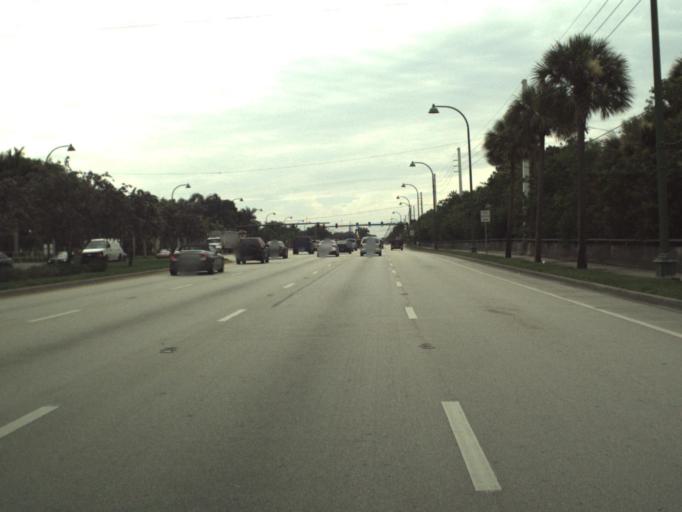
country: US
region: Florida
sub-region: Palm Beach County
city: Wellington
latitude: 26.6812
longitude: -80.2328
